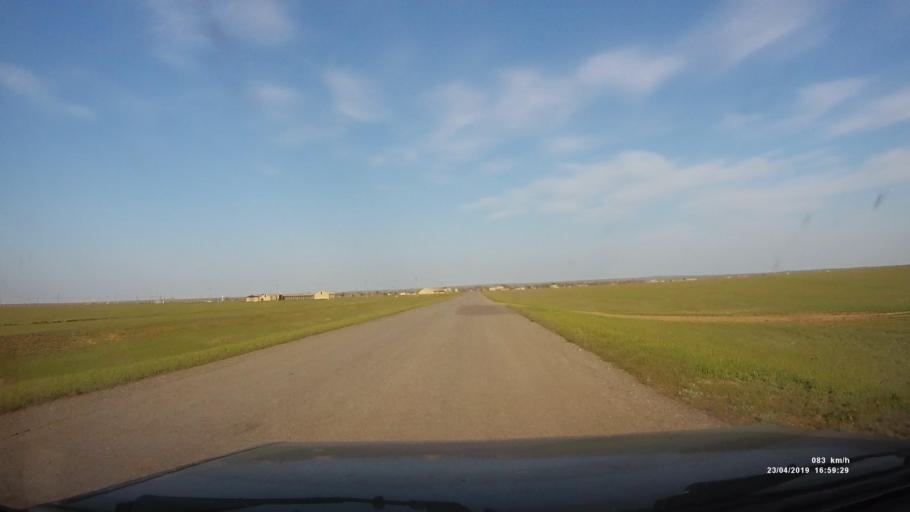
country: RU
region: Kalmykiya
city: Priyutnoye
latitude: 46.3088
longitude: 43.3912
